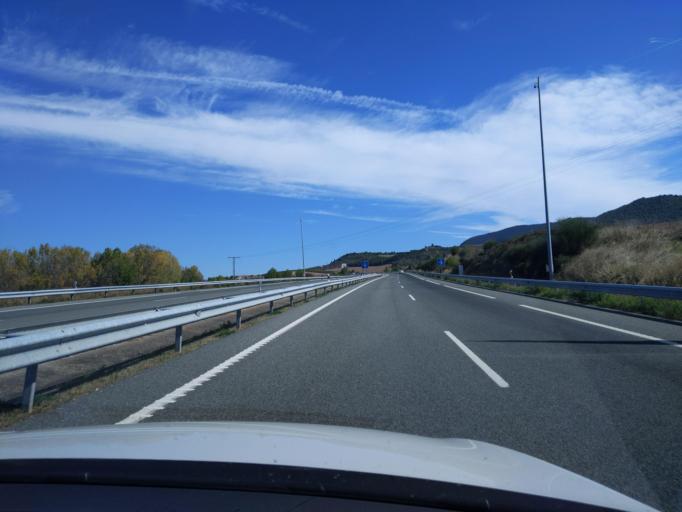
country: ES
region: Navarre
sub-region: Provincia de Navarra
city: Villamayor de Monjardin
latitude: 42.6179
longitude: -2.1062
